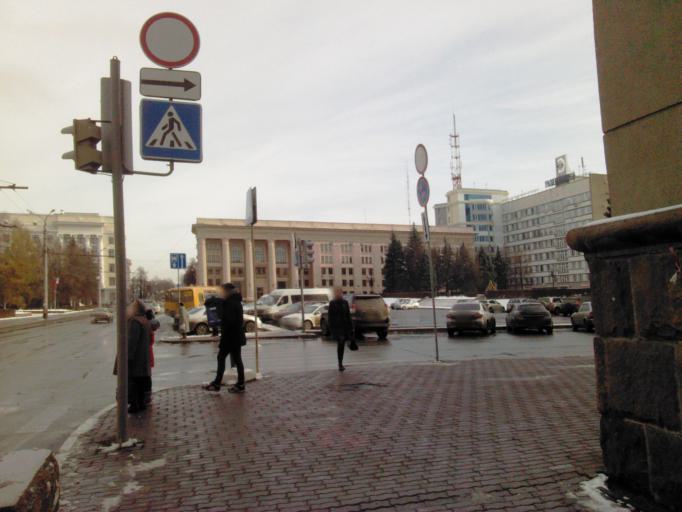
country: RU
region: Chelyabinsk
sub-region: Gorod Chelyabinsk
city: Chelyabinsk
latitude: 55.1575
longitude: 61.4013
